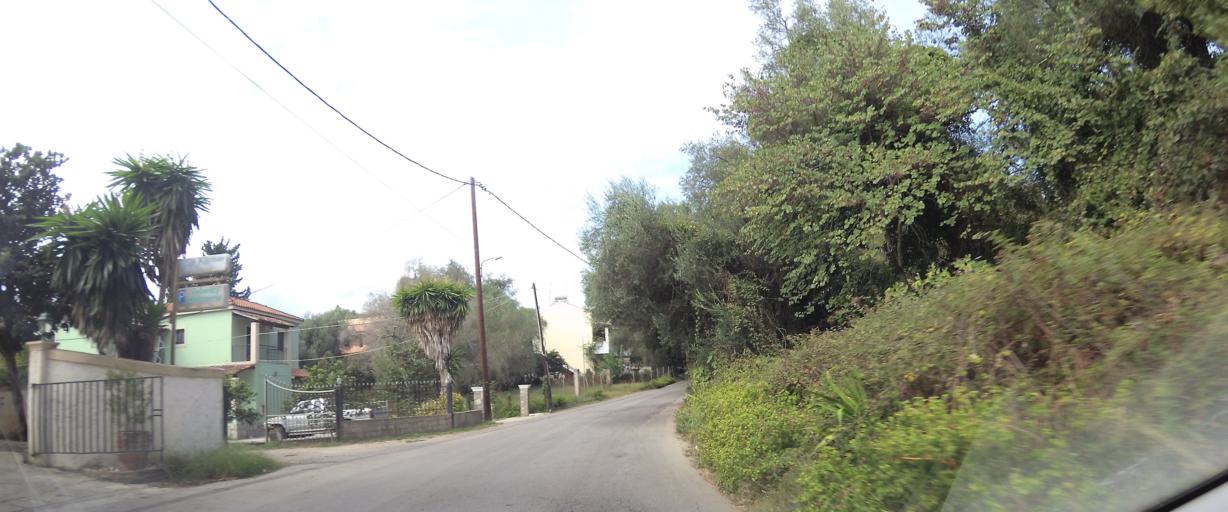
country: GR
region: Ionian Islands
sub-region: Nomos Kerkyras
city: Kontokali
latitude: 39.6874
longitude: 19.8317
